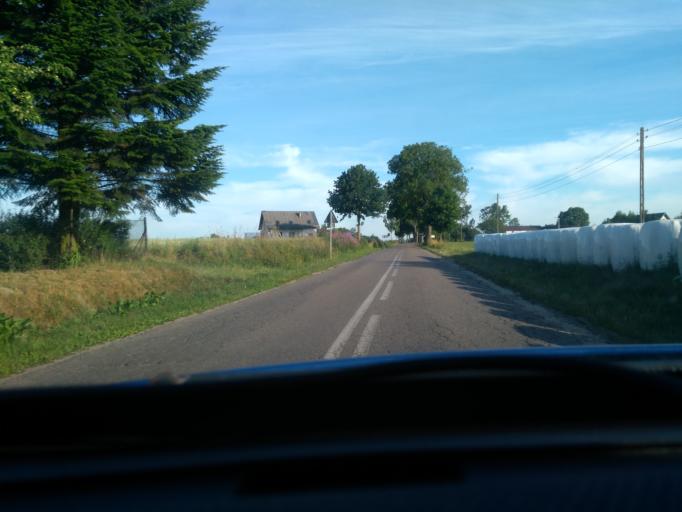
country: PL
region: Pomeranian Voivodeship
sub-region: Powiat kartuski
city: Przodkowo
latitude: 54.3959
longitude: 18.3389
